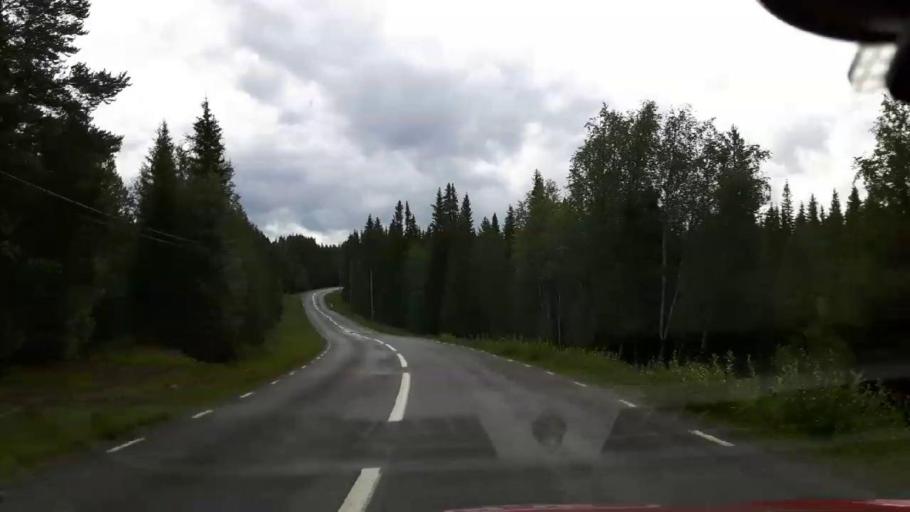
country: NO
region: Nord-Trondelag
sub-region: Lierne
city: Sandvika
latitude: 64.5104
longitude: 14.1562
